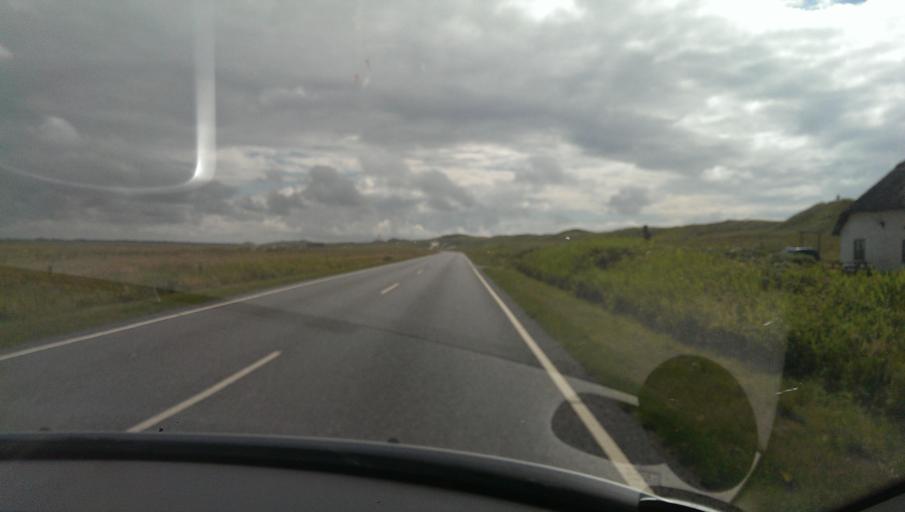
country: DK
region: Central Jutland
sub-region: Ringkobing-Skjern Kommune
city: Ringkobing
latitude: 56.1904
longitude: 8.1273
